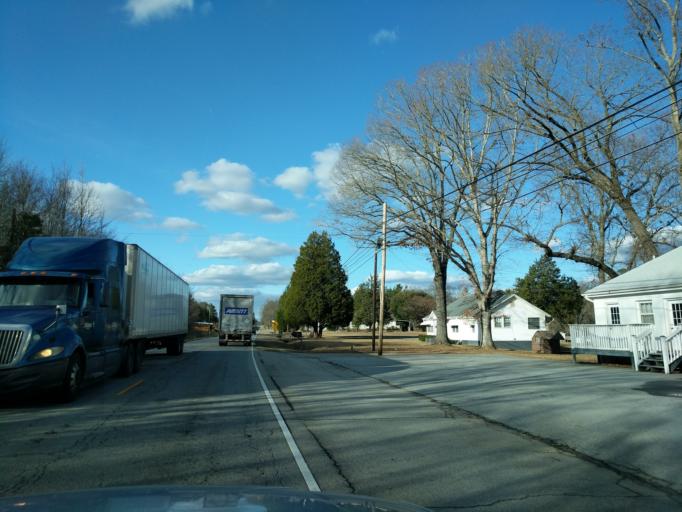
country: US
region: South Carolina
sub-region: Spartanburg County
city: Woodruff
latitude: 34.7157
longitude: -82.0221
